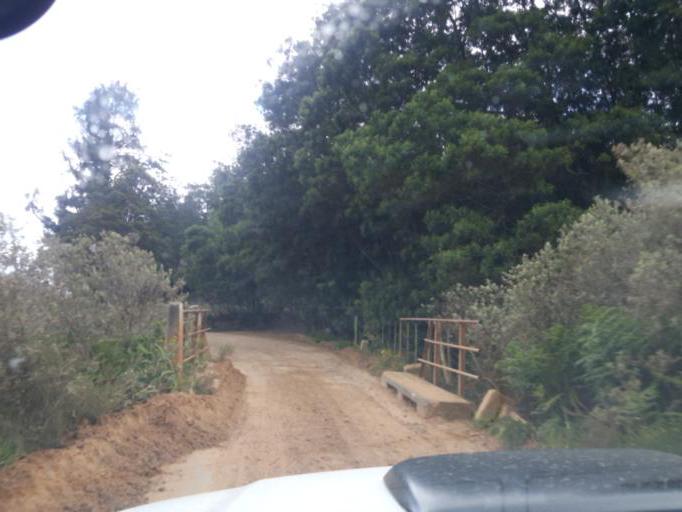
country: ZA
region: Western Cape
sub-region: Eden District Municipality
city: George
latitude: -33.8704
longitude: 22.4468
